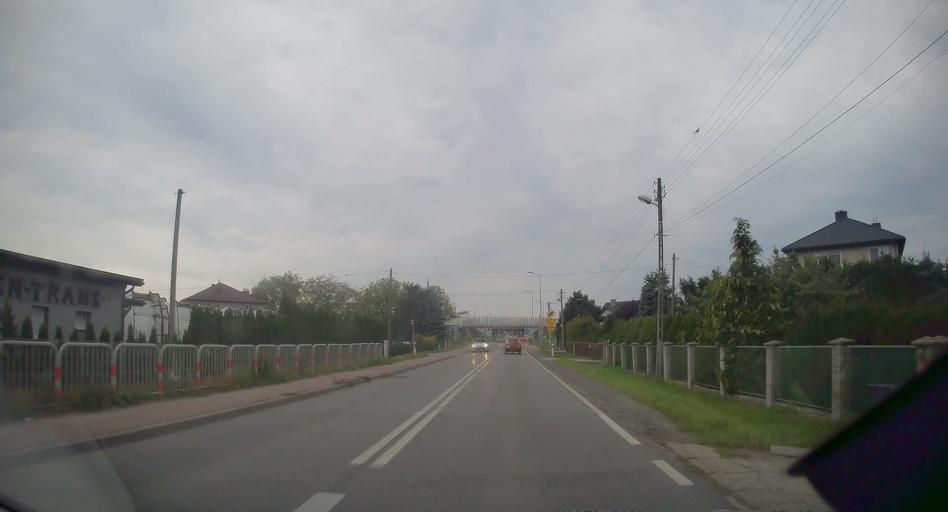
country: PL
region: Lesser Poland Voivodeship
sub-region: Powiat wielicki
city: Podleze
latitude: 50.0130
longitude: 20.1577
